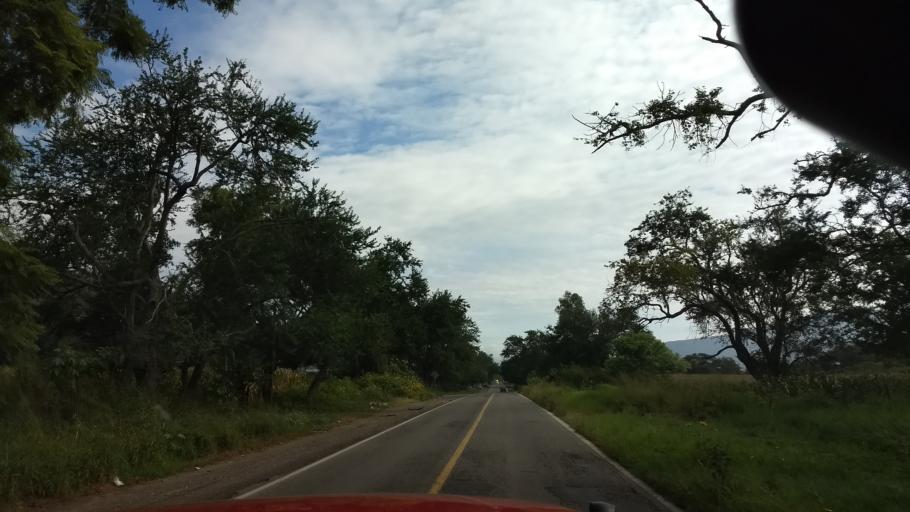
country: MX
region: Jalisco
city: Tuxpan
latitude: 19.5454
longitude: -103.4006
